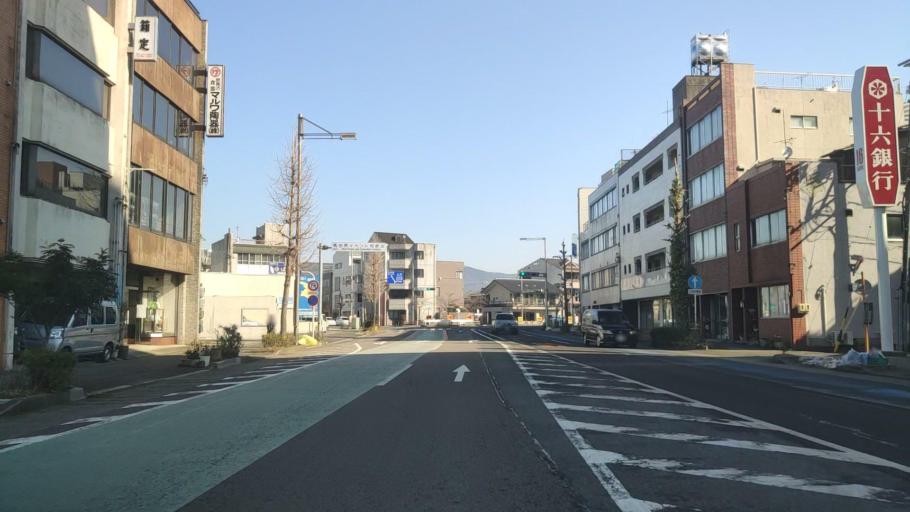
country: JP
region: Gifu
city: Gifu-shi
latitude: 35.4310
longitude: 136.7649
